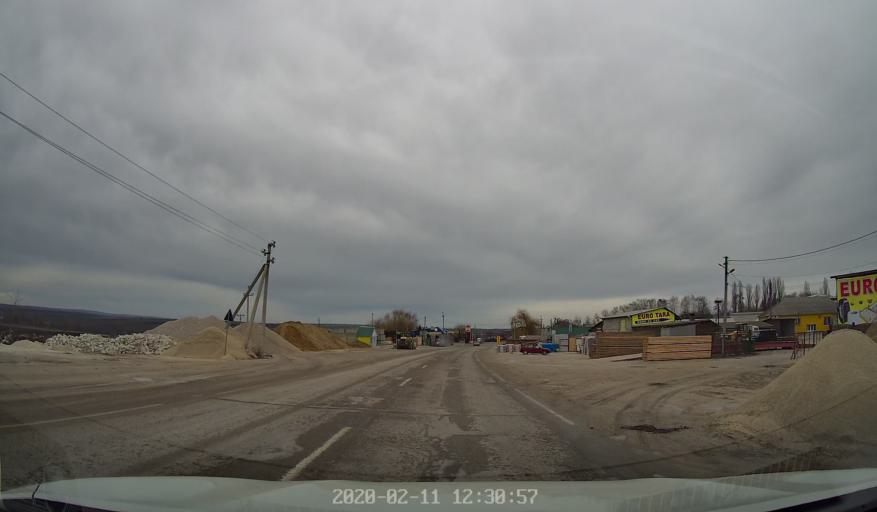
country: MD
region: Raionul Edinet
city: Edinet
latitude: 48.1698
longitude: 27.2798
